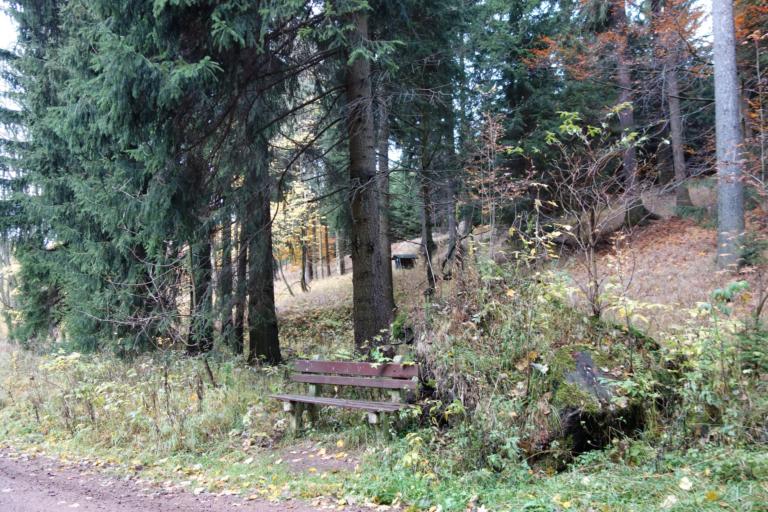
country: DE
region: Saxony
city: Altenberg
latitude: 50.7257
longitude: 13.7137
